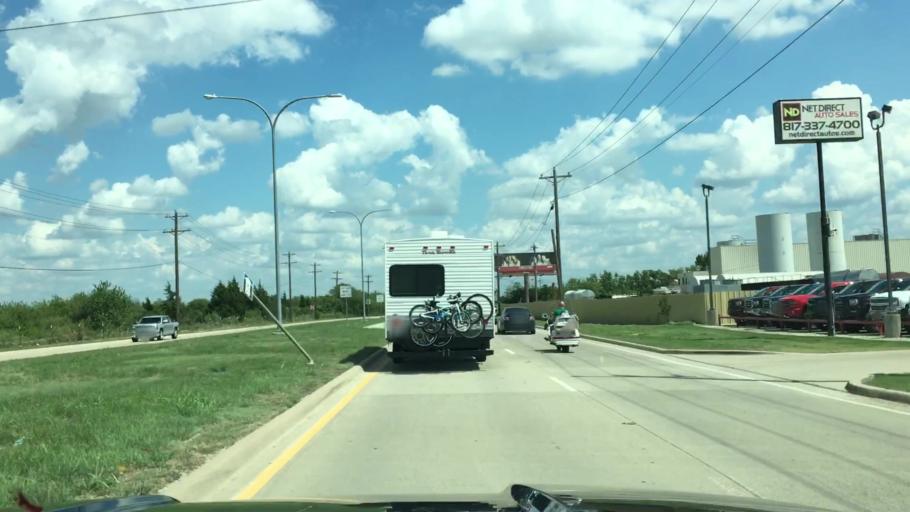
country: US
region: Texas
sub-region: Tarrant County
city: Keller
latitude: 32.9319
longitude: -97.3026
